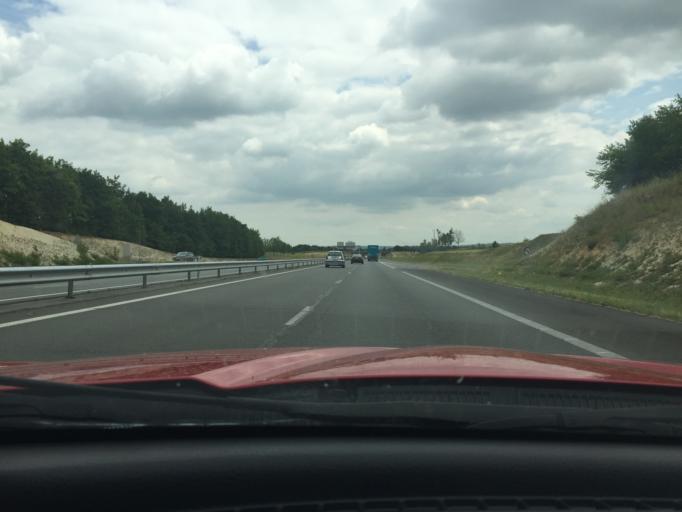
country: FR
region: Picardie
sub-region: Departement de l'Aisne
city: Athies-sous-Laon
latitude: 49.6070
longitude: 3.6568
